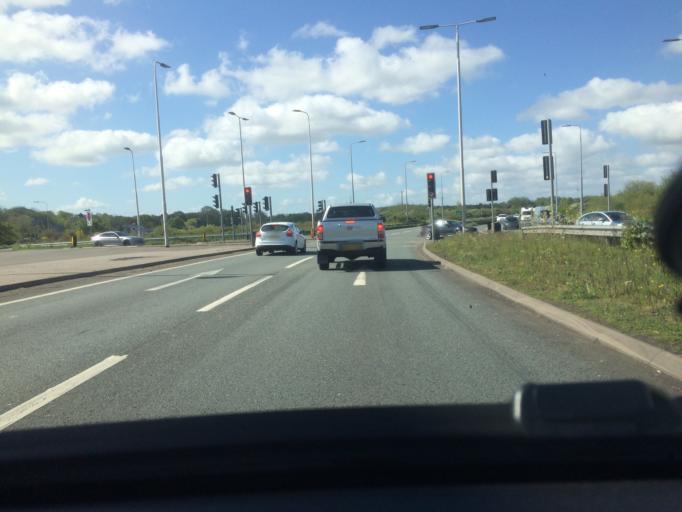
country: GB
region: England
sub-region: Cheshire West and Chester
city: Eccleston
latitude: 53.1514
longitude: -2.9168
